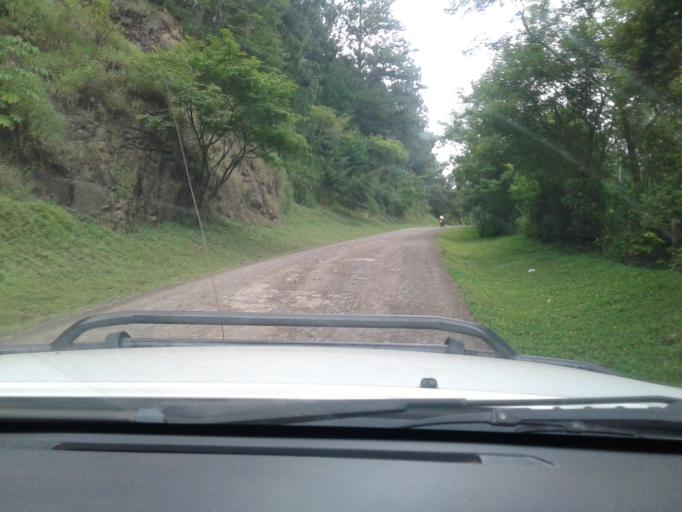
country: NI
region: Matagalpa
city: San Ramon
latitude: 12.9145
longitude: -85.7810
